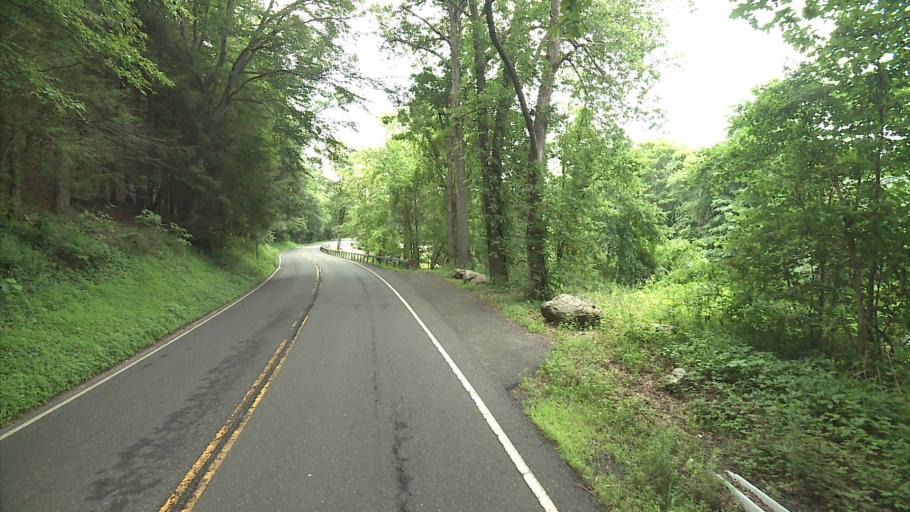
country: US
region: Connecticut
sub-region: Litchfield County
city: New Milford
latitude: 41.5645
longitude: -73.3274
